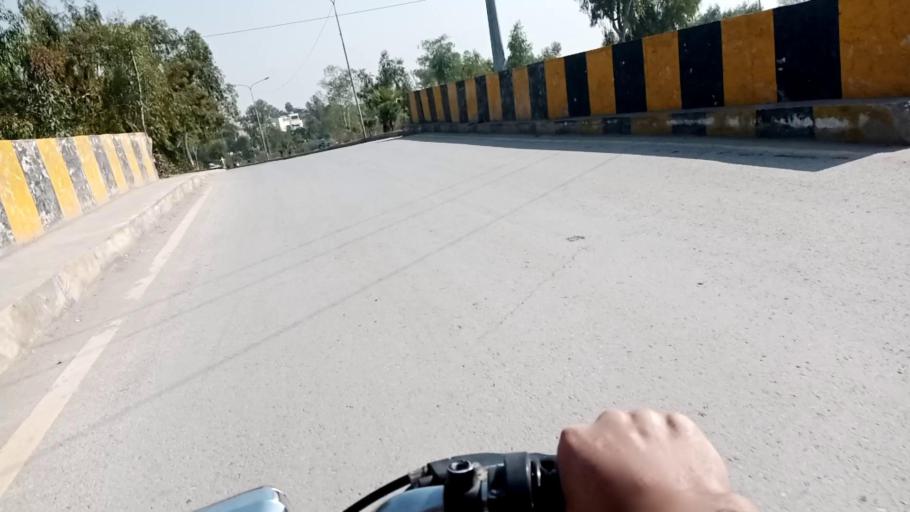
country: PK
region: Khyber Pakhtunkhwa
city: Peshawar
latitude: 33.9637
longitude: 71.4300
